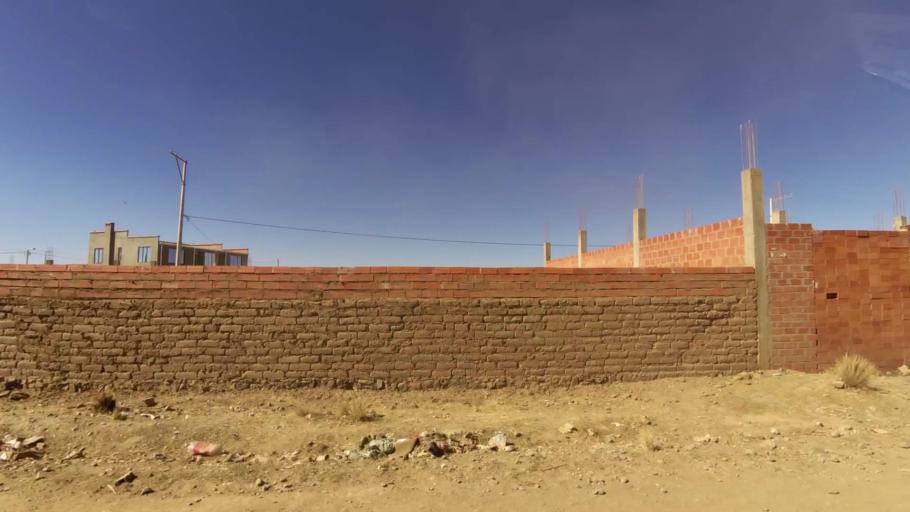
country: BO
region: La Paz
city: La Paz
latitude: -16.6257
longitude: -68.1947
